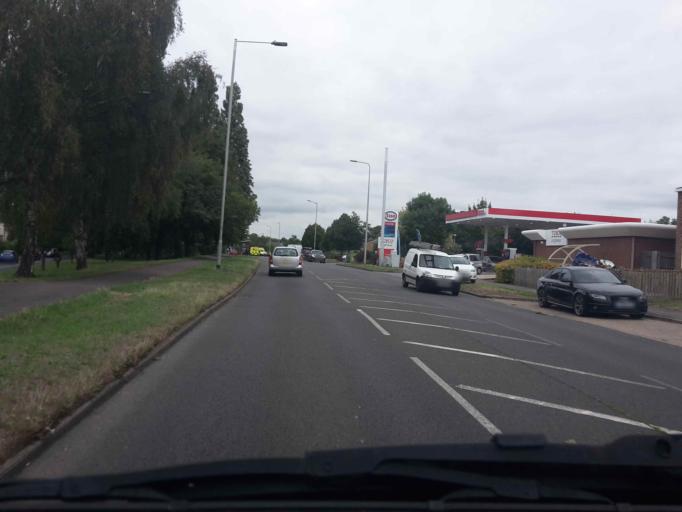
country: GB
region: England
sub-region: Reading
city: Reading
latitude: 51.4783
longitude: -0.9657
